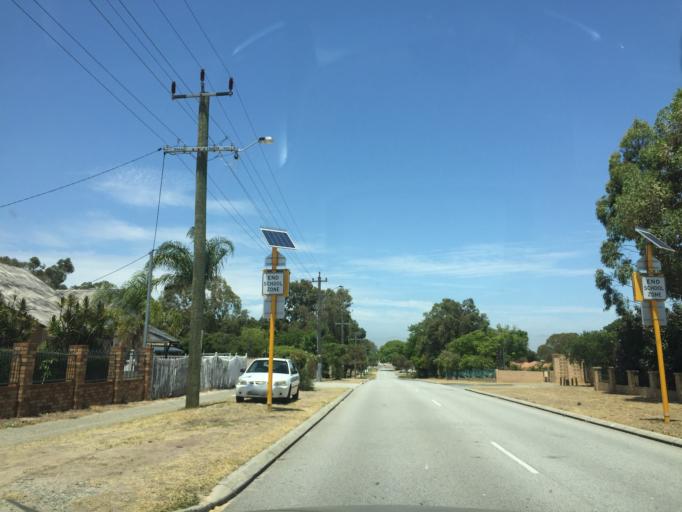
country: AU
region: Western Australia
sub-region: Canning
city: Queens Park
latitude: -32.0001
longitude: 115.9437
